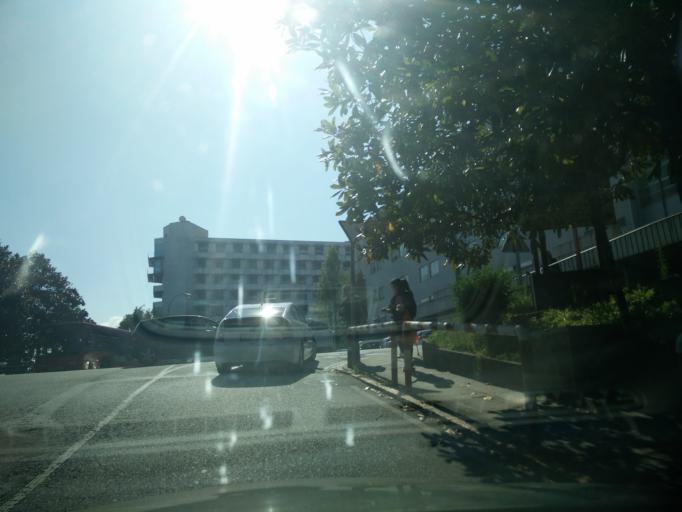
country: ES
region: Galicia
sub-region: Provincia da Coruna
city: A Coruna
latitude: 43.3441
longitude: -8.3876
